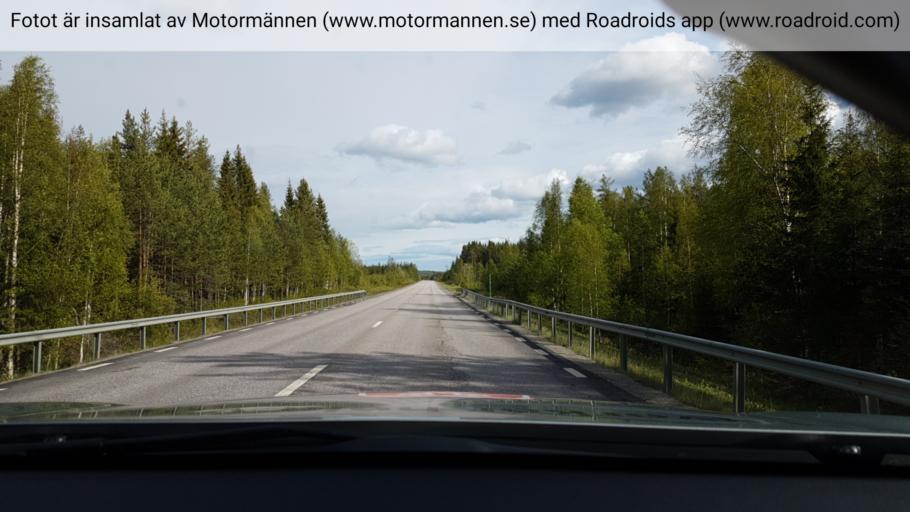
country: SE
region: Vaesterbotten
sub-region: Vannas Kommun
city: Vaennaes
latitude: 63.9103
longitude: 19.6636
